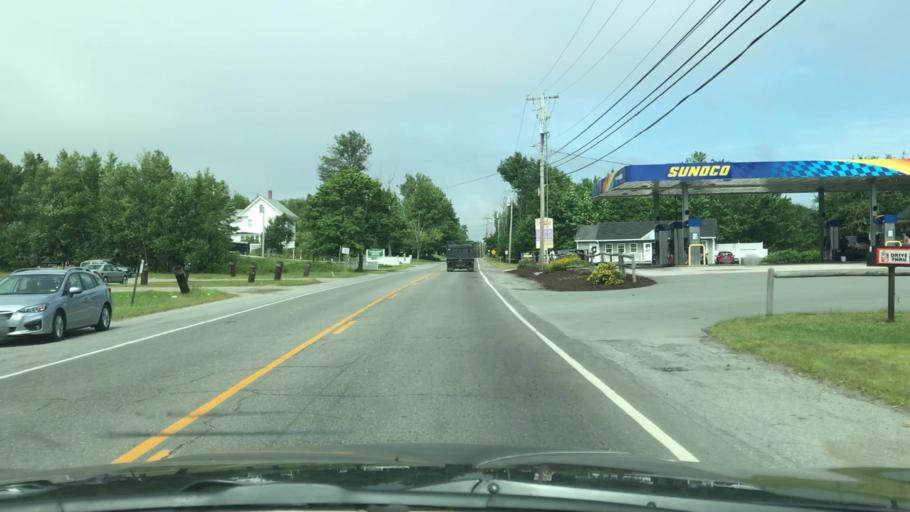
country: US
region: Maine
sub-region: Waldo County
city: Stockton Springs
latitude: 44.4607
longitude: -68.9102
